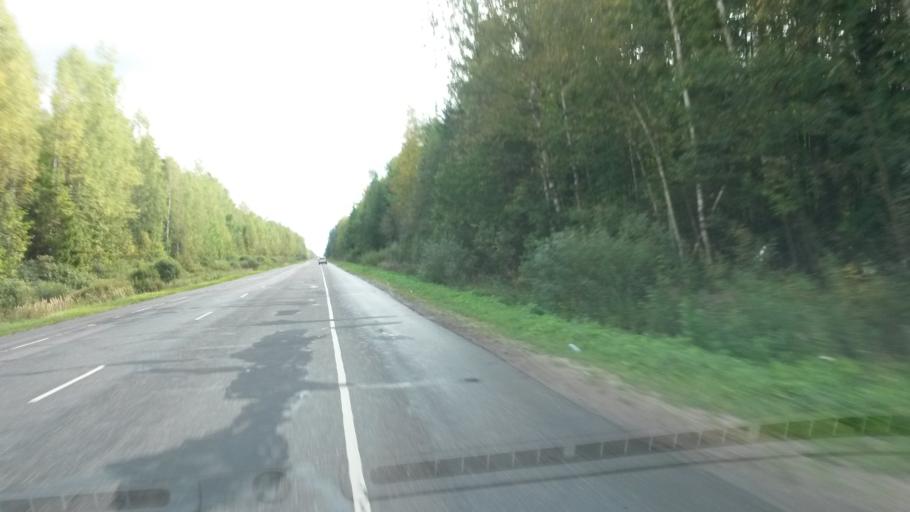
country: RU
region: Ivanovo
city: Kaminskiy
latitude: 57.0770
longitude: 41.4782
